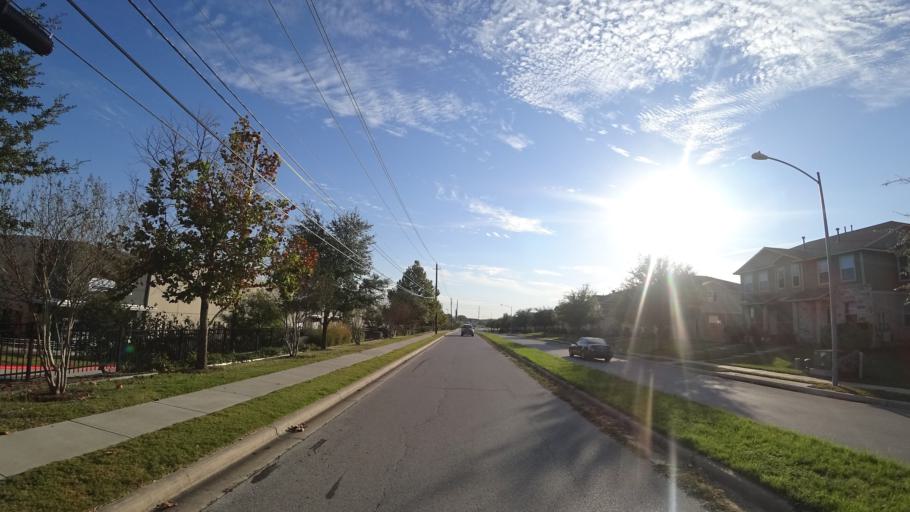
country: US
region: Texas
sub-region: Travis County
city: Pflugerville
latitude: 30.4126
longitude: -97.6465
